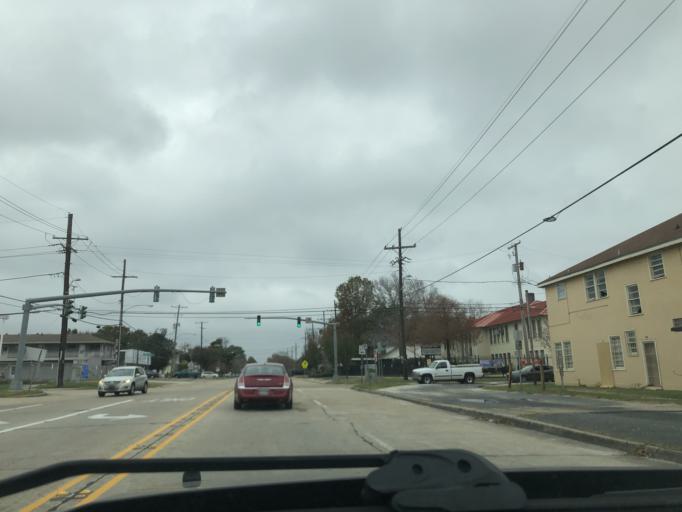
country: US
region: Louisiana
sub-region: Jefferson Parish
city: Metairie Terrace
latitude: 29.9754
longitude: -90.1606
